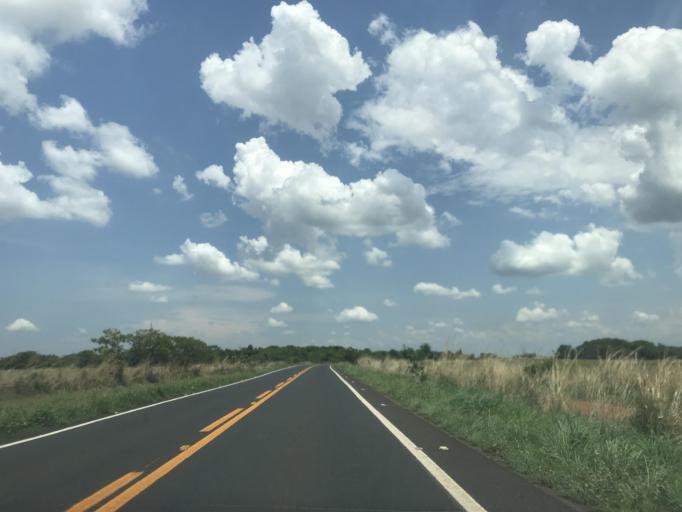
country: BR
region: Goias
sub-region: Piracanjuba
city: Piracanjuba
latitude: -17.4385
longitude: -48.7857
